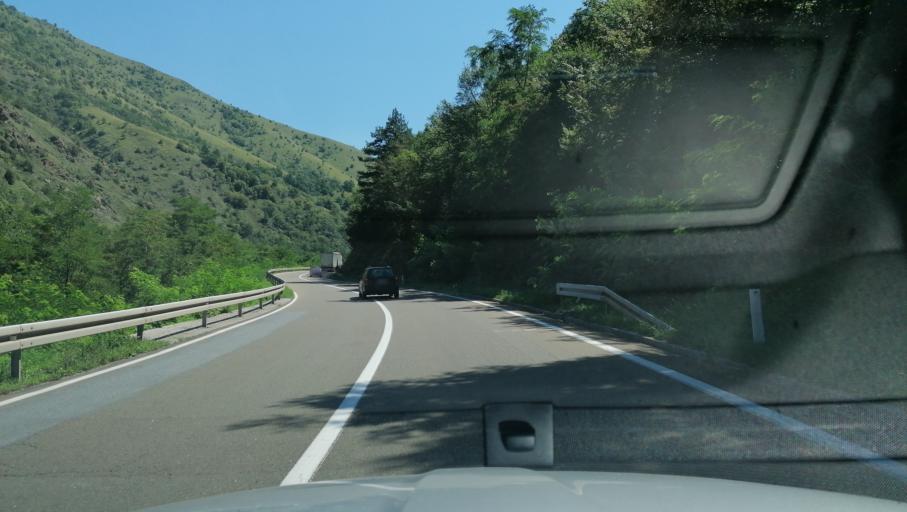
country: RS
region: Central Serbia
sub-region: Raski Okrug
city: Kraljevo
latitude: 43.5759
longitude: 20.5884
